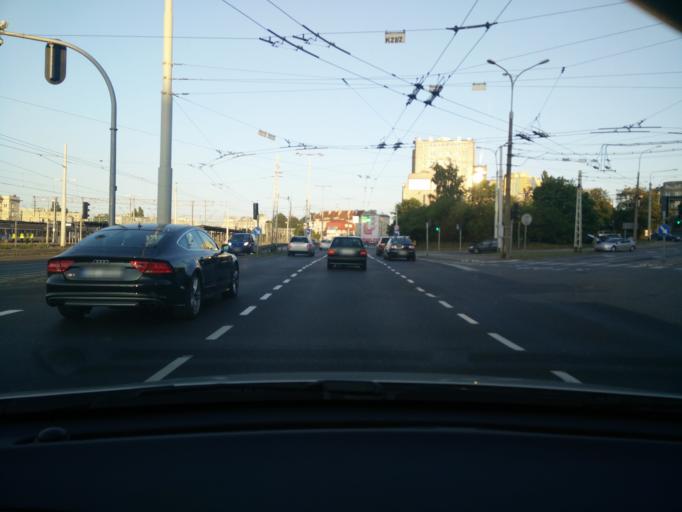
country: PL
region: Pomeranian Voivodeship
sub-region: Gdynia
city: Gdynia
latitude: 54.5213
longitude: 18.5265
